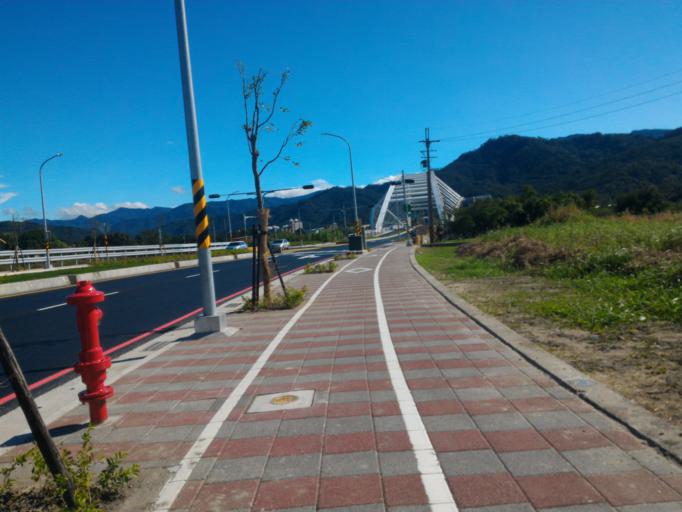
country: TW
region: Taiwan
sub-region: Taoyuan
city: Taoyuan
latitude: 24.9394
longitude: 121.3866
